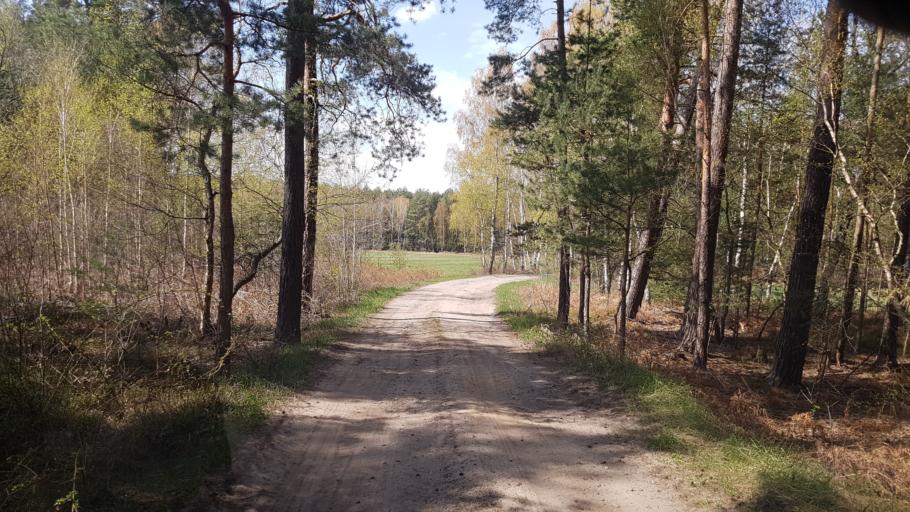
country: DE
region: Brandenburg
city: Ruckersdorf
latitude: 51.5534
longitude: 13.6304
